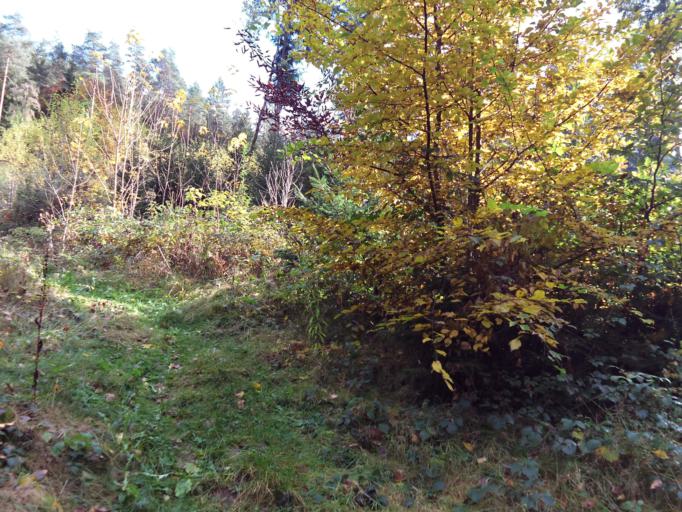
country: DE
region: Rheinland-Pfalz
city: Fischbach
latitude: 49.4680
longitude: 7.9534
